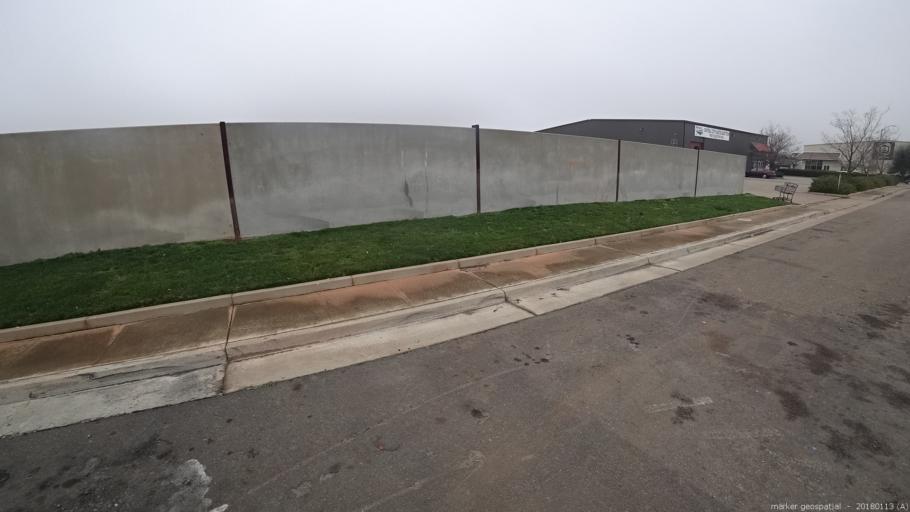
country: US
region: California
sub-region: Sacramento County
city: Rancho Cordova
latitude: 38.5641
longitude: -121.2533
